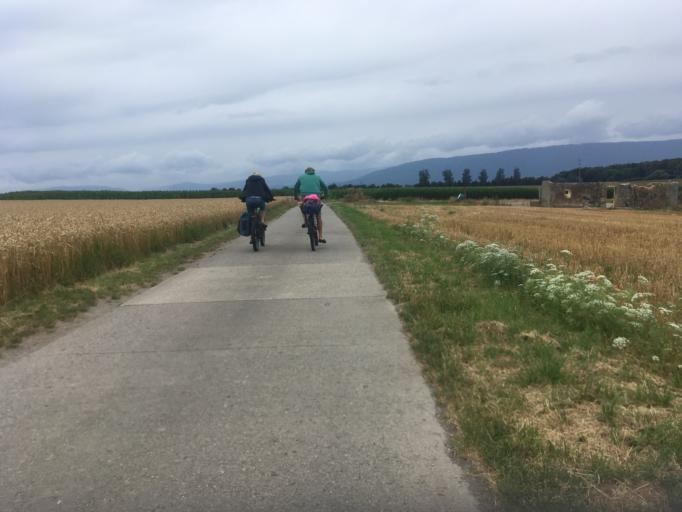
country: CH
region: Fribourg
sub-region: See District
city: Bas-Vully
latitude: 46.9704
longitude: 7.0998
